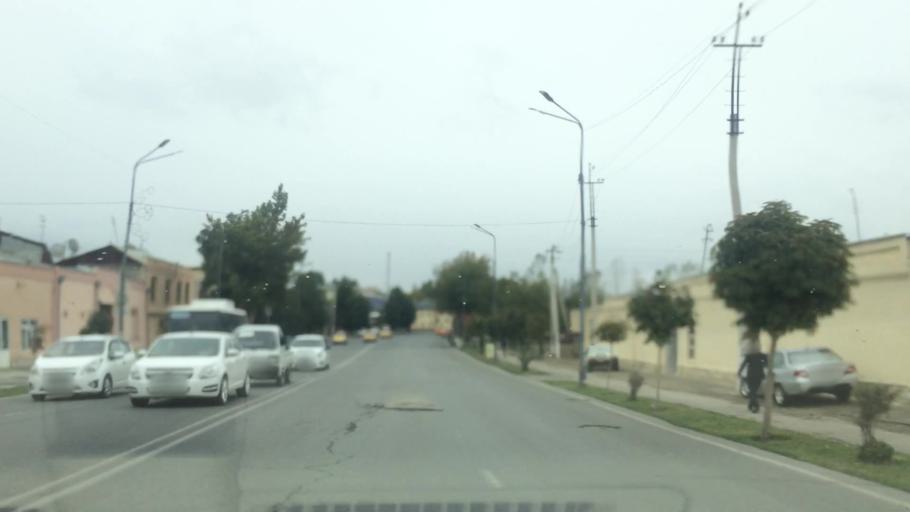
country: UZ
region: Samarqand
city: Samarqand
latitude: 39.6572
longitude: 66.9709
